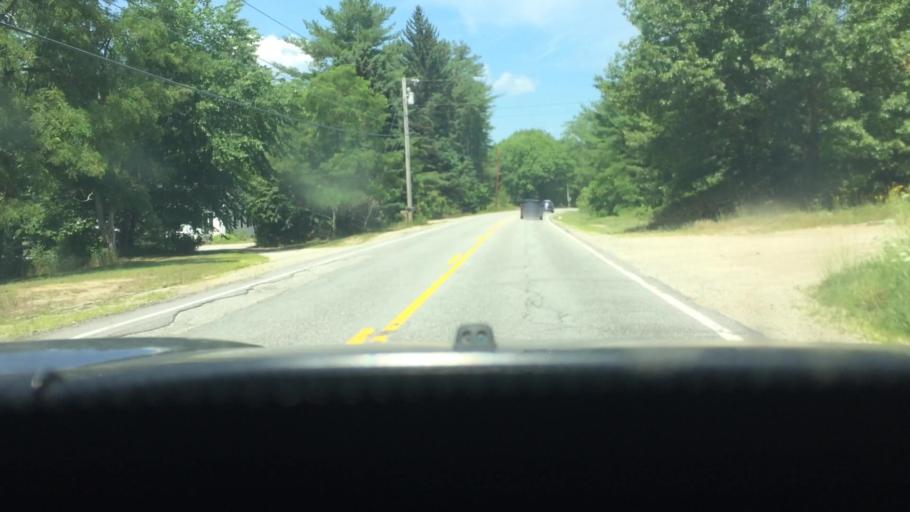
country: US
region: Maine
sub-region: Androscoggin County
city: Mechanic Falls
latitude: 44.1199
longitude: -70.4302
